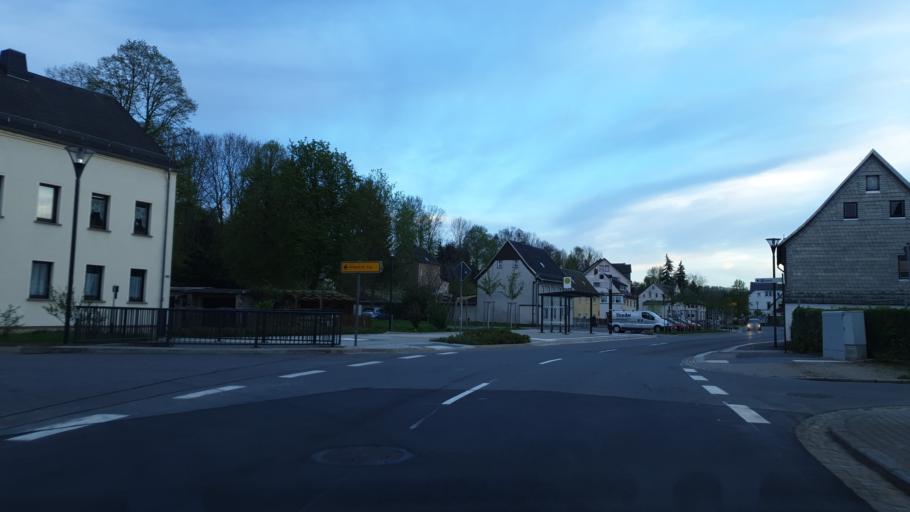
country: DE
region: Saxony
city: Gersdorf
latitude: 50.7591
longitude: 12.7085
